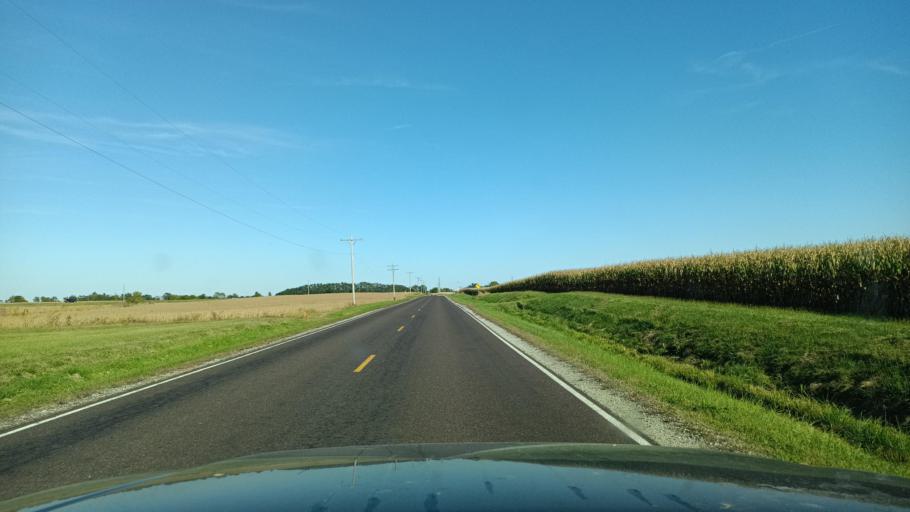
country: US
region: Illinois
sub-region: De Witt County
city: Clinton
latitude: 40.2316
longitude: -88.9769
